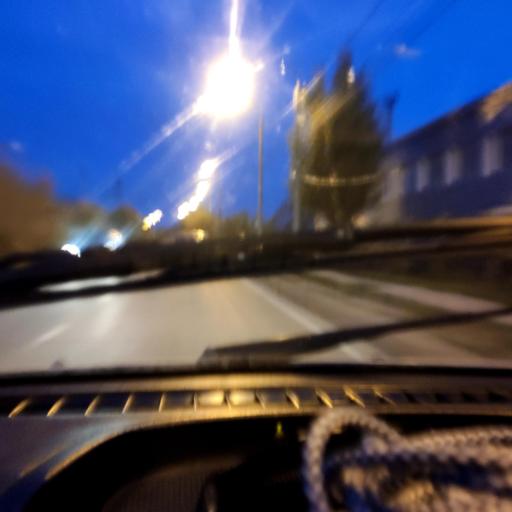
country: RU
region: Samara
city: Zhigulevsk
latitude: 53.4630
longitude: 49.5700
